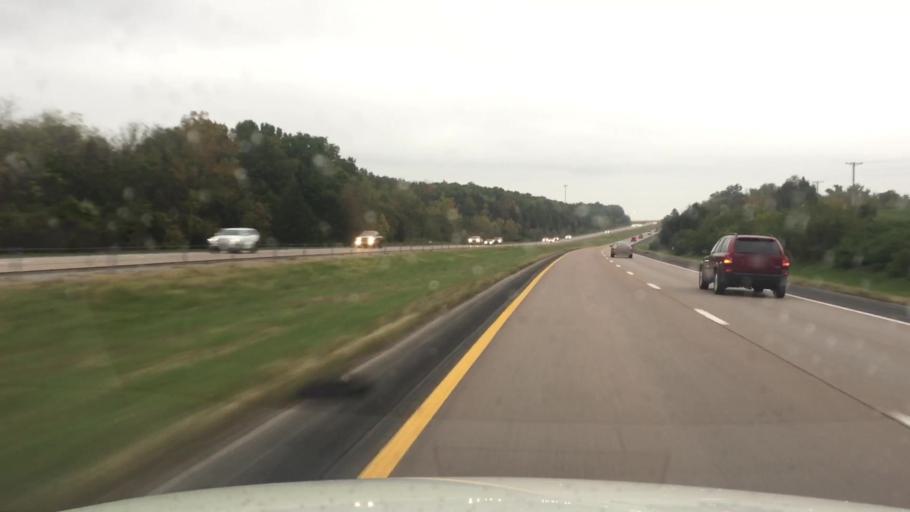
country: US
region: Missouri
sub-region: Boone County
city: Ashland
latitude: 38.8198
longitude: -92.2512
